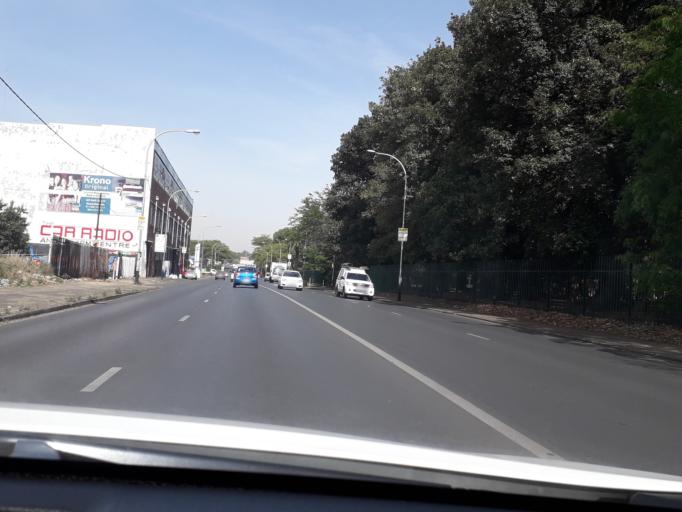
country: ZA
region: Gauteng
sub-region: City of Johannesburg Metropolitan Municipality
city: Johannesburg
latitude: -26.1967
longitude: 28.0267
